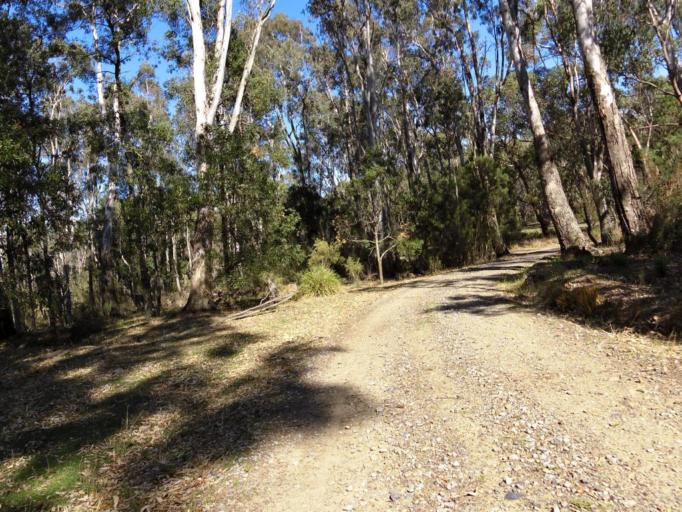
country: AU
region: Victoria
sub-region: Yarra Ranges
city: Lysterfield
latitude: -37.9473
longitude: 145.2855
